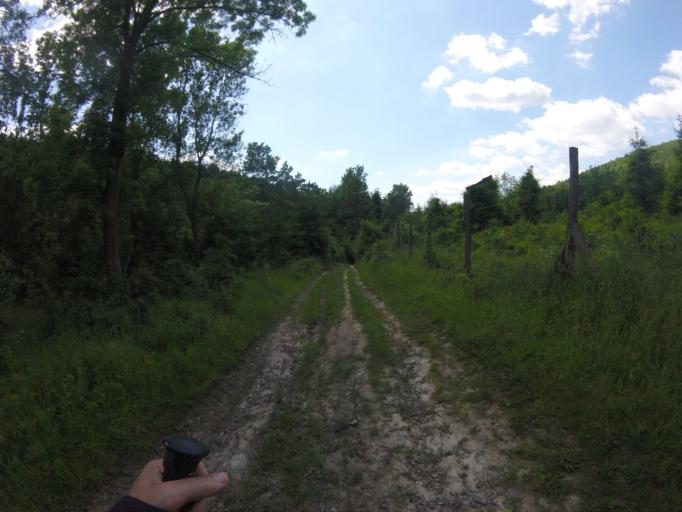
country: HU
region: Nograd
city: Matraverebely
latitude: 47.9425
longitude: 19.7907
